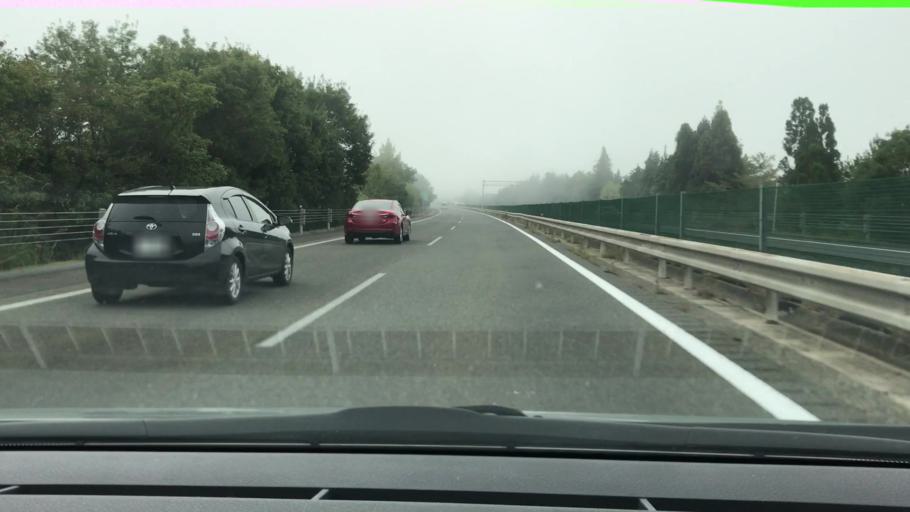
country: JP
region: Hyogo
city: Sasayama
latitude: 35.0749
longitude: 135.1711
